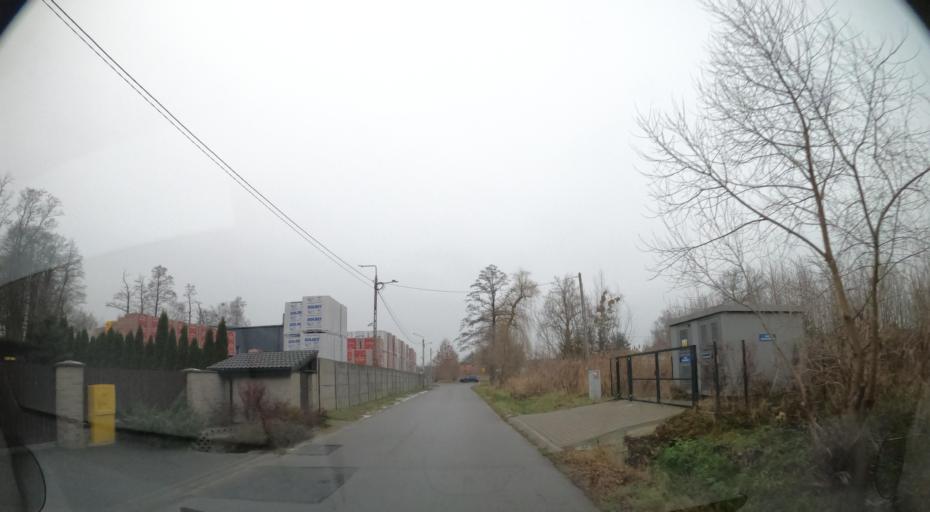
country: PL
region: Masovian Voivodeship
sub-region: Powiat radomski
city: Jastrzebia
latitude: 51.4257
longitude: 21.2271
